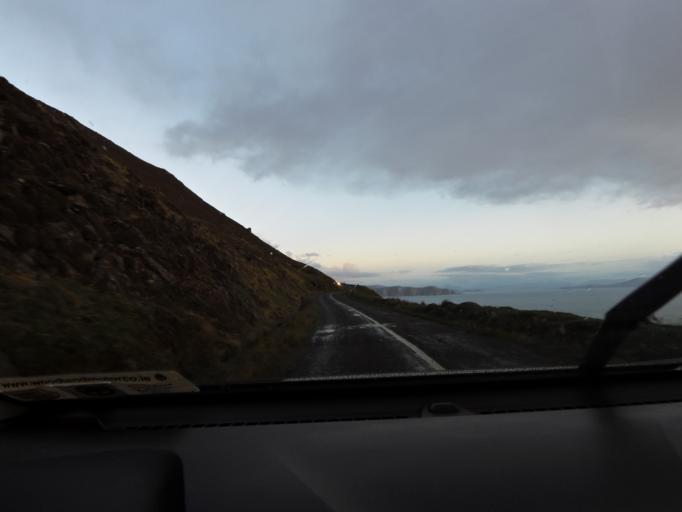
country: IE
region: Connaught
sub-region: Maigh Eo
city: Belmullet
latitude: 53.9704
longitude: -10.1796
